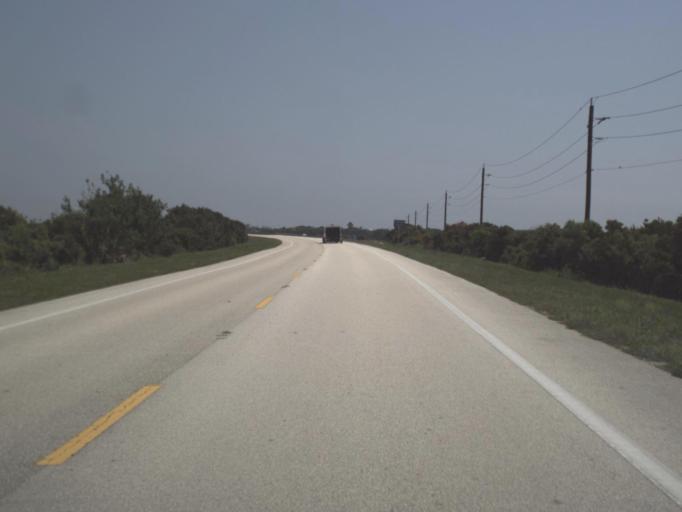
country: US
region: Florida
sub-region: Saint Johns County
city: Butler Beach
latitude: 29.7617
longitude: -81.2659
